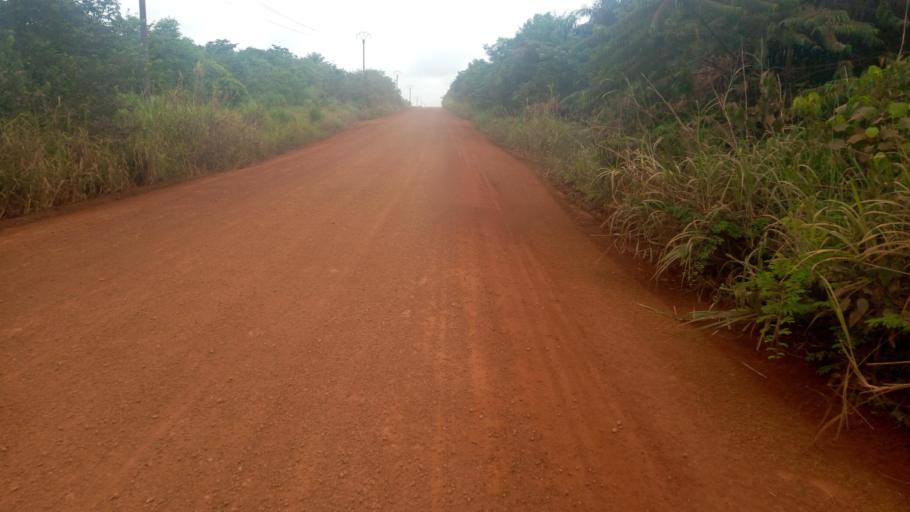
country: SL
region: Southern Province
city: Mogbwemo
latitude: 7.7115
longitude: -12.2849
